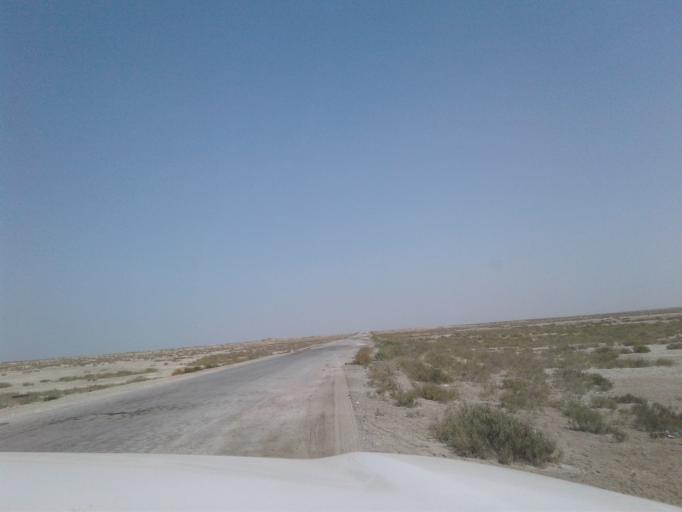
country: IR
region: Golestan
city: Gomishan
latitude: 37.9348
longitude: 53.8465
